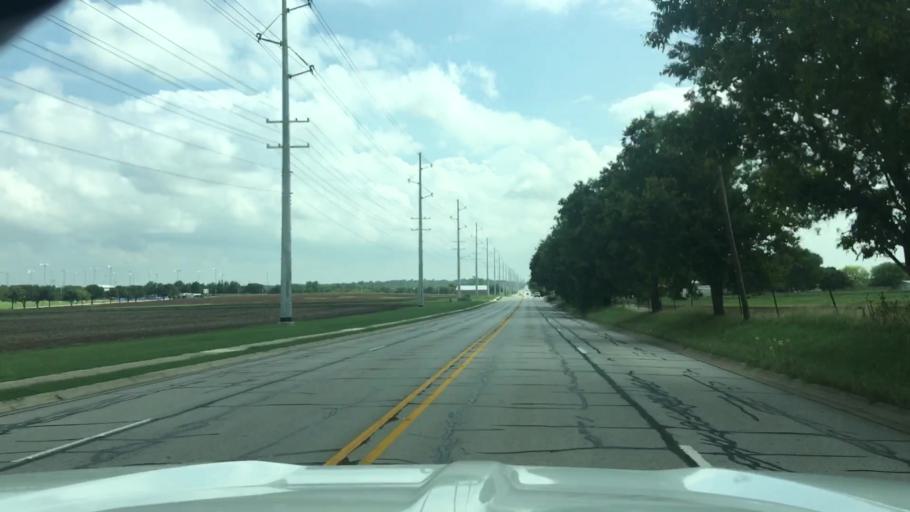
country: US
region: Texas
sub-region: Denton County
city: Denton
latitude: 33.2469
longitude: -97.1606
